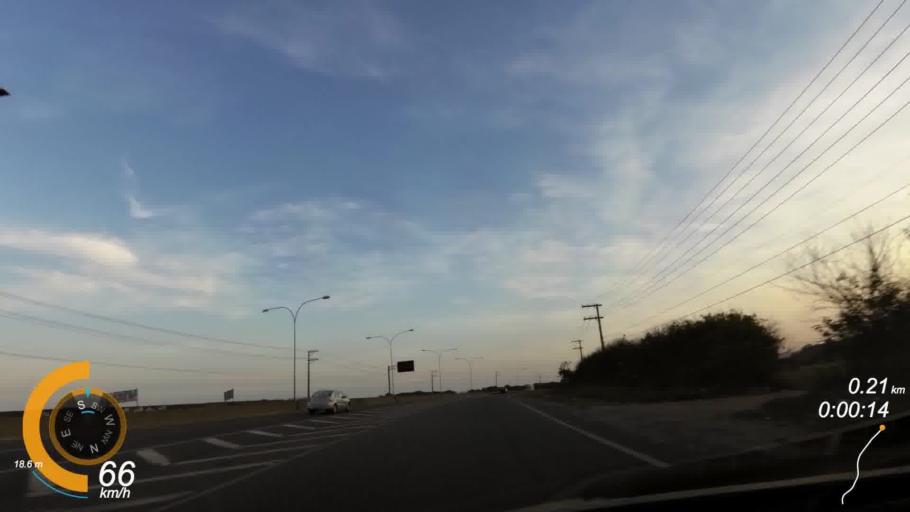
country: BR
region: Espirito Santo
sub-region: Vila Velha
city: Vila Velha
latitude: -20.4498
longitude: -40.3346
